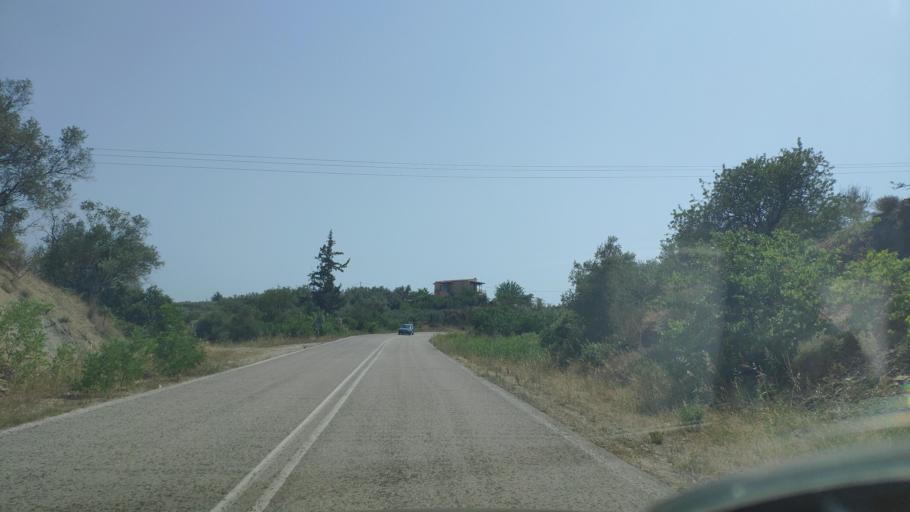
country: GR
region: Epirus
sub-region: Nomos Artas
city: Peta
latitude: 39.1694
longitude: 21.0548
